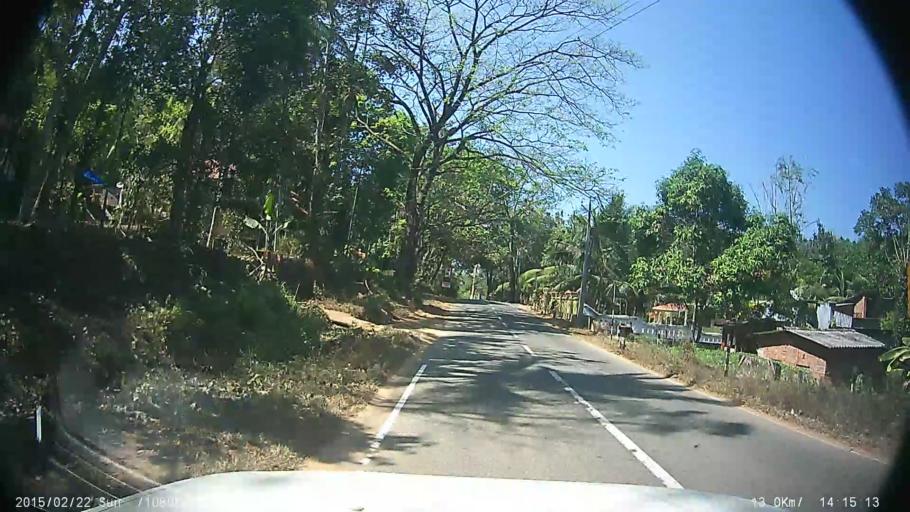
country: IN
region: Kerala
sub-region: Kottayam
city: Kottayam
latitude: 9.5480
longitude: 76.6845
